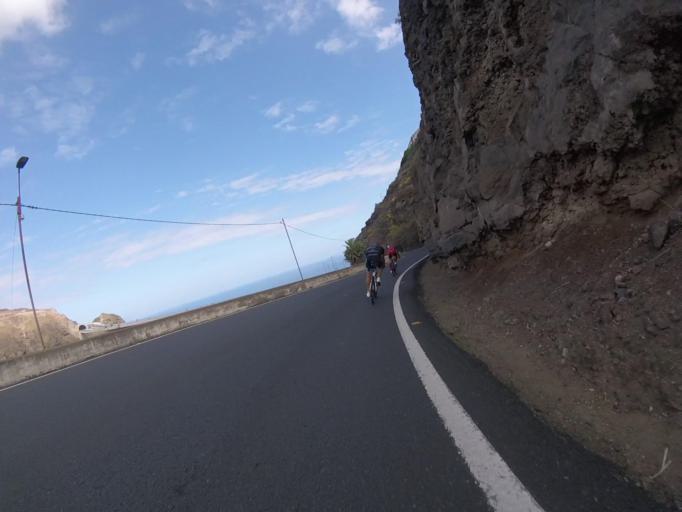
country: ES
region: Canary Islands
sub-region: Provincia de Las Palmas
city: Guia
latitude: 28.1375
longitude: -15.5969
